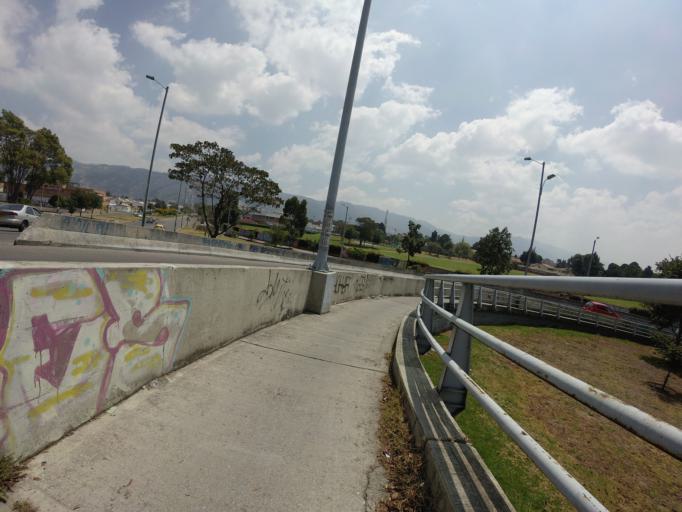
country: CO
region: Bogota D.C.
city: Barrio San Luis
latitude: 4.7374
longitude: -74.0480
